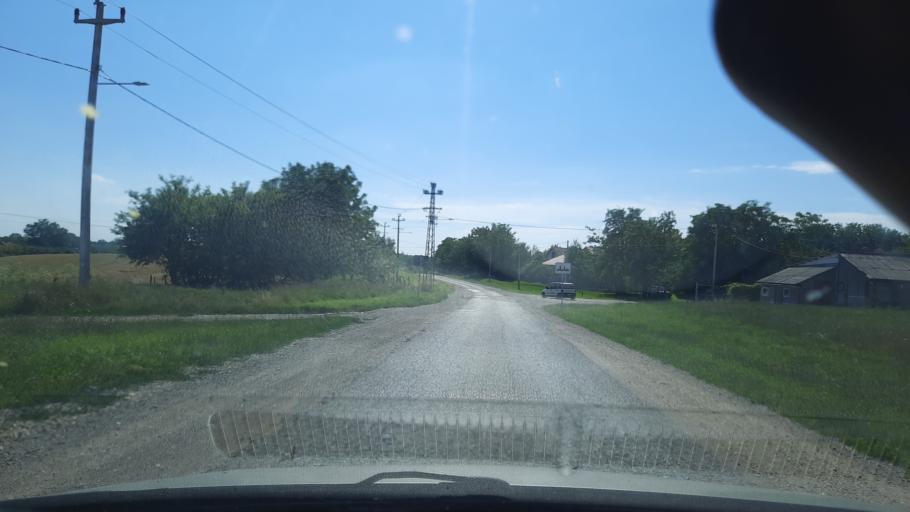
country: RS
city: Cortanovci
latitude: 45.1137
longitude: 19.9528
